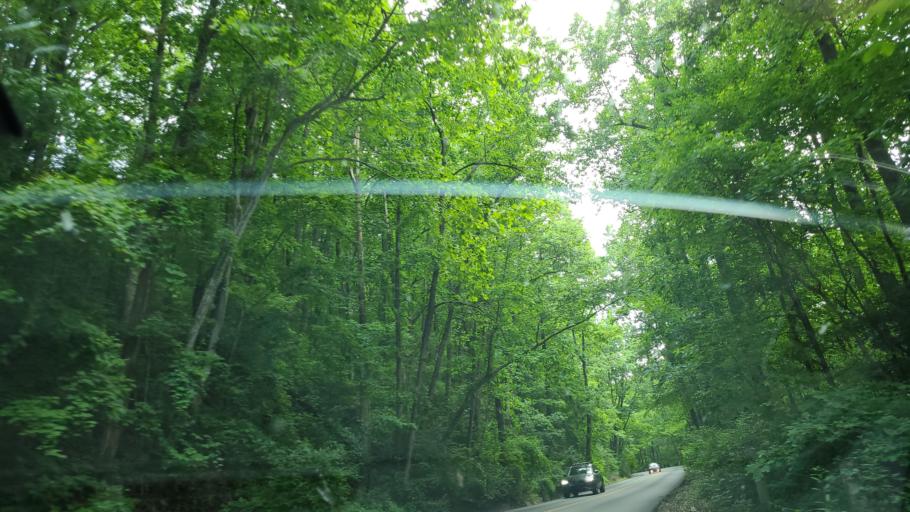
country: US
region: Tennessee
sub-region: Hamilton County
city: Lookout Mountain
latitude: 34.9880
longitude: -85.3479
